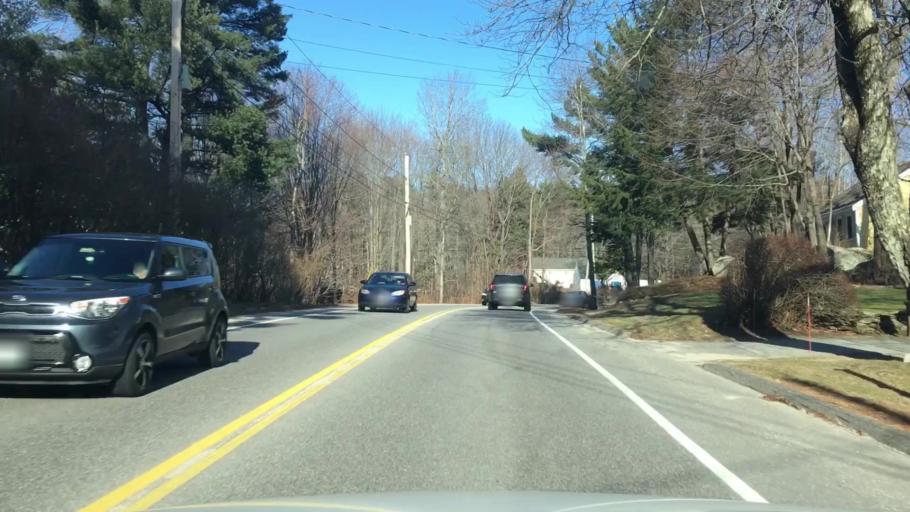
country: US
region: Maine
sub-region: Cumberland County
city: Falmouth
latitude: 43.7201
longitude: -70.2640
